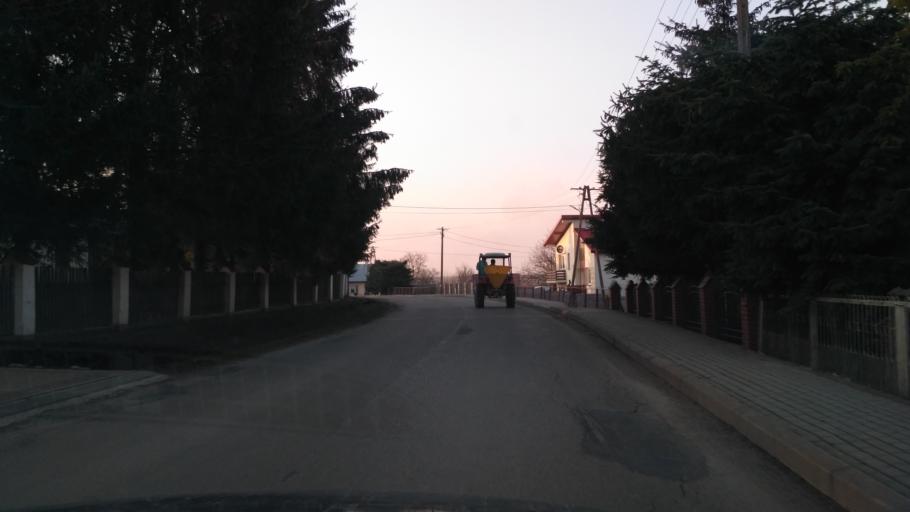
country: PL
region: Subcarpathian Voivodeship
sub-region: Powiat przeworski
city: Zarzecze
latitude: 49.9663
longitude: 22.5571
